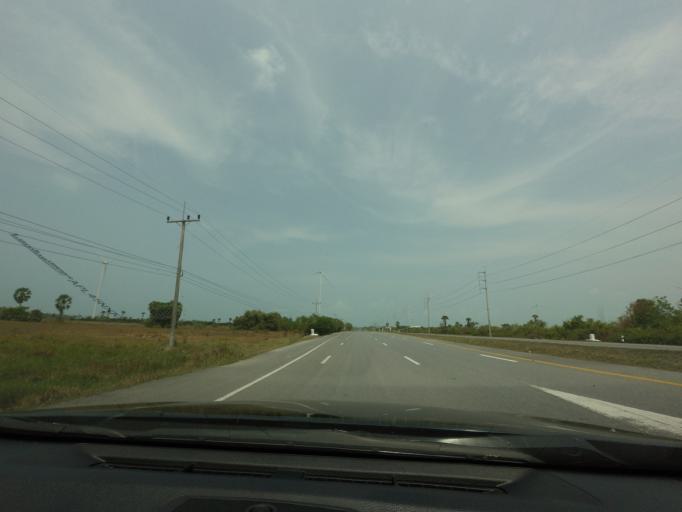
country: TH
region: Nakhon Si Thammarat
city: Hua Sai
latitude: 7.9973
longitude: 100.3115
